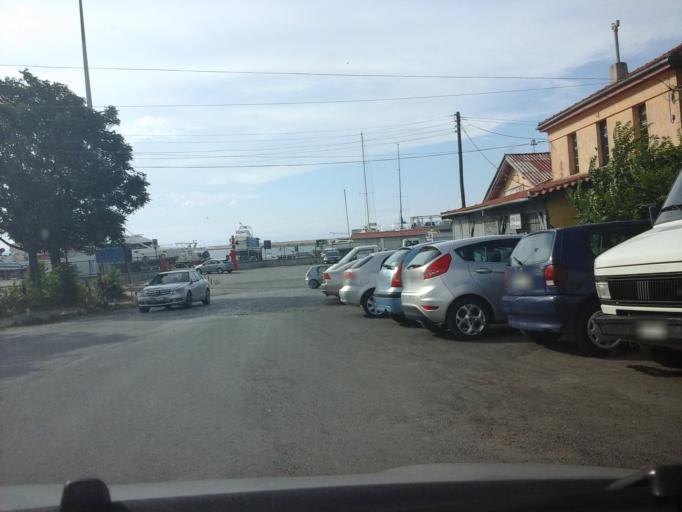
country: GR
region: East Macedonia and Thrace
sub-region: Nomos Evrou
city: Alexandroupoli
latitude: 40.8450
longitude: 25.8781
